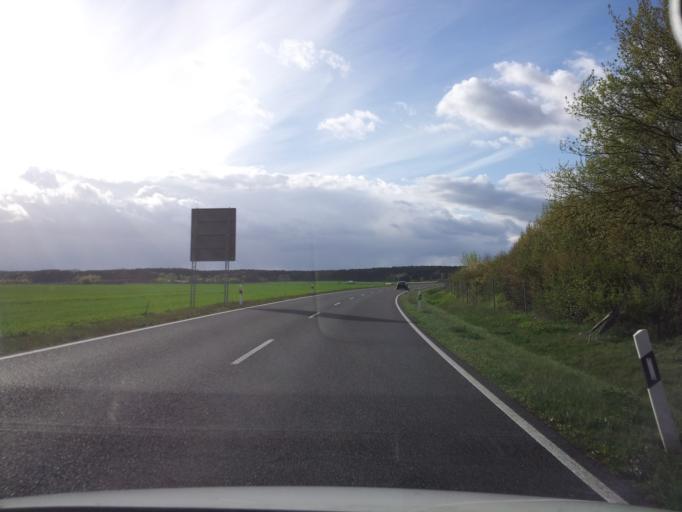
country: DE
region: Brandenburg
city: Schenkendobern
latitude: 51.8916
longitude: 14.6567
